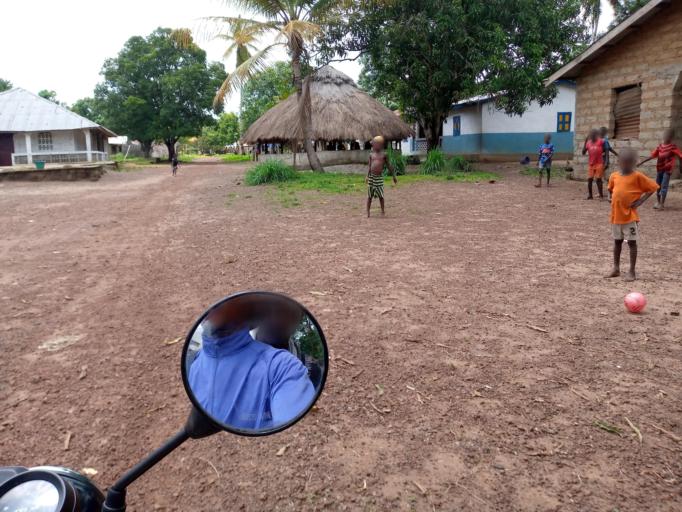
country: SL
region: Northern Province
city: Mange
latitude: 8.9734
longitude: -12.8289
